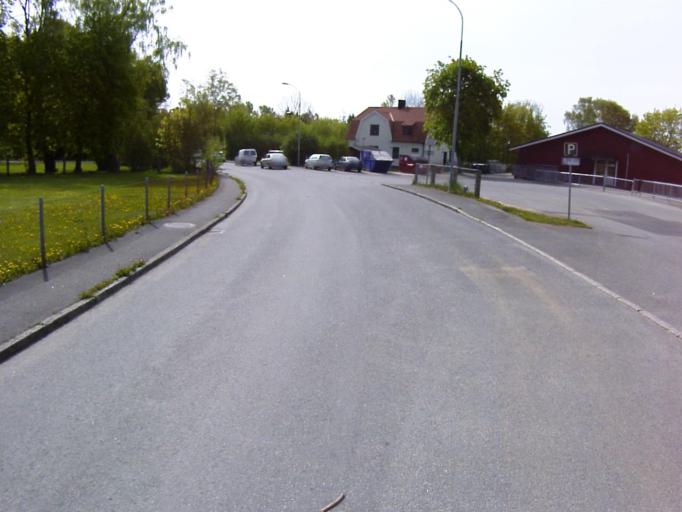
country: SE
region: Skane
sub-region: Kristianstads Kommun
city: Fjalkinge
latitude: 56.0367
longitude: 14.2757
